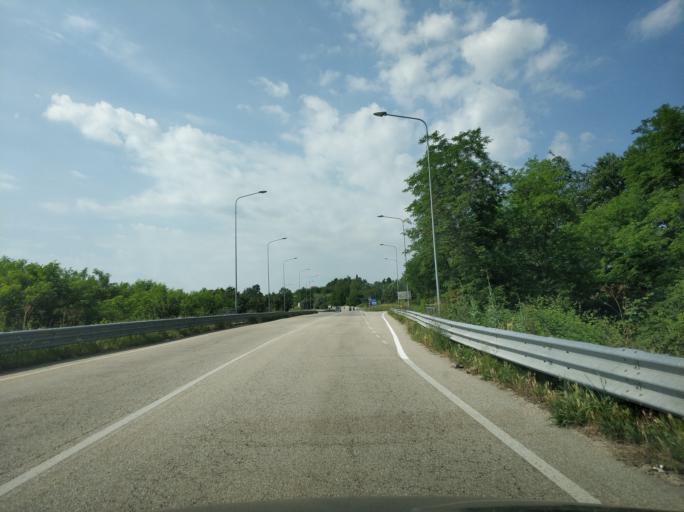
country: IT
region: Piedmont
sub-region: Provincia di Cuneo
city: Monta
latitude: 44.8182
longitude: 7.9480
